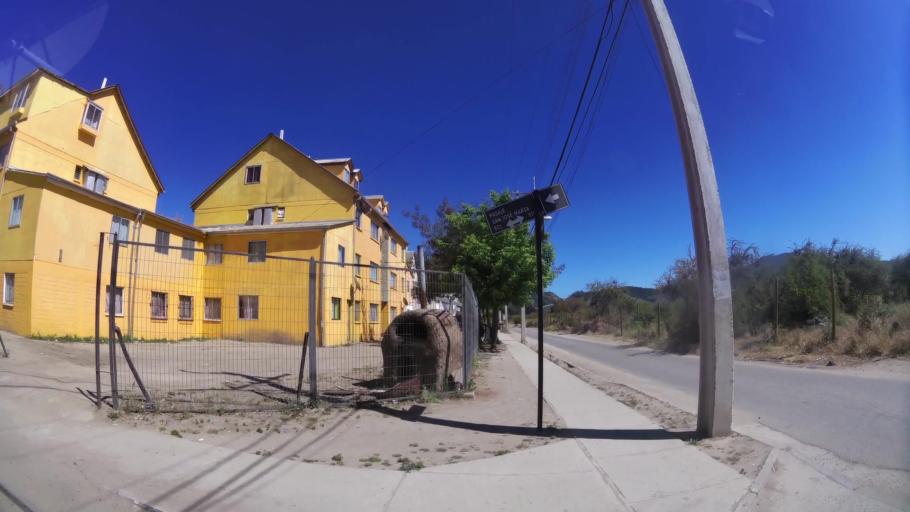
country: CL
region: Valparaiso
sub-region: Provincia de Marga Marga
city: Quilpue
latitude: -33.3044
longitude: -71.4139
